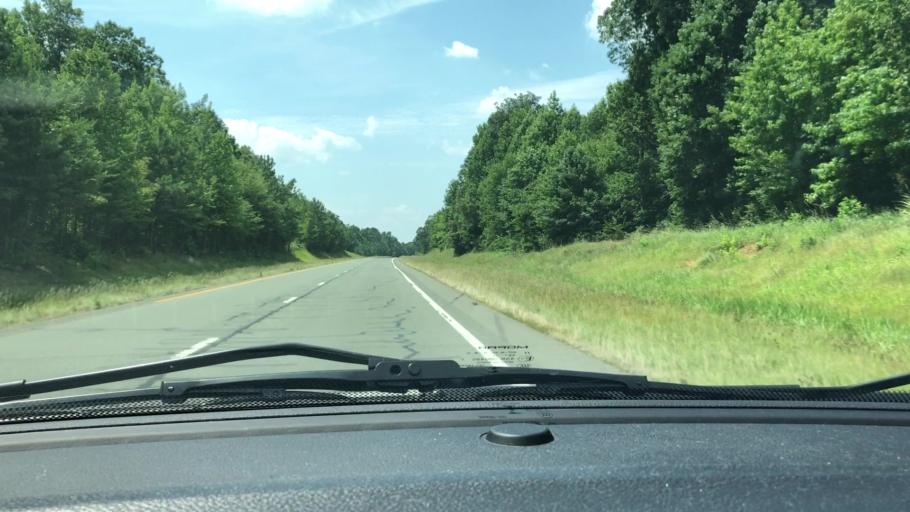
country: US
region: North Carolina
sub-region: Chatham County
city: Siler City
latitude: 35.7825
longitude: -79.5123
